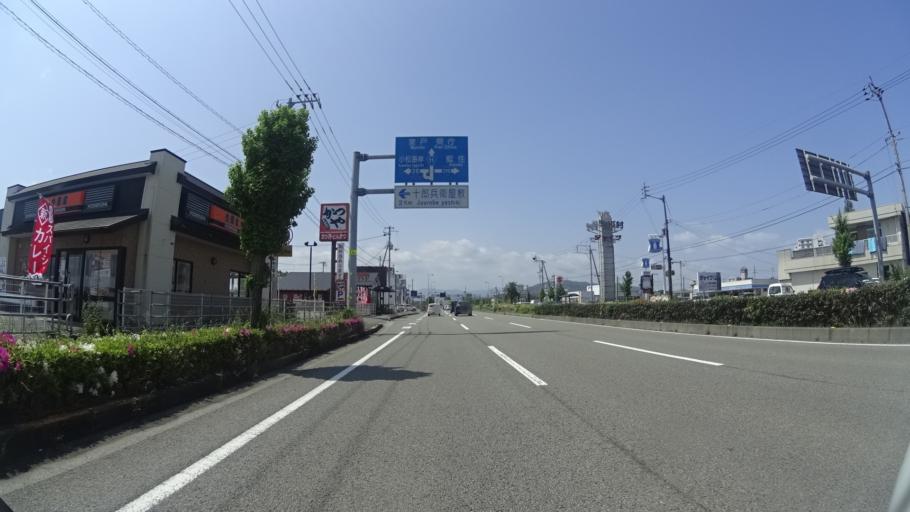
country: JP
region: Tokushima
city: Tokushima-shi
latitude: 34.0981
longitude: 134.5739
